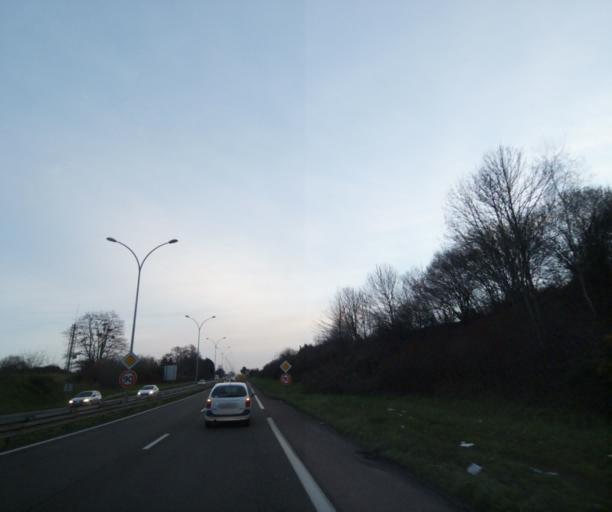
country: FR
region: Pays de la Loire
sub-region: Departement de la Sarthe
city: Le Mans
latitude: 48.0093
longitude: 0.1714
